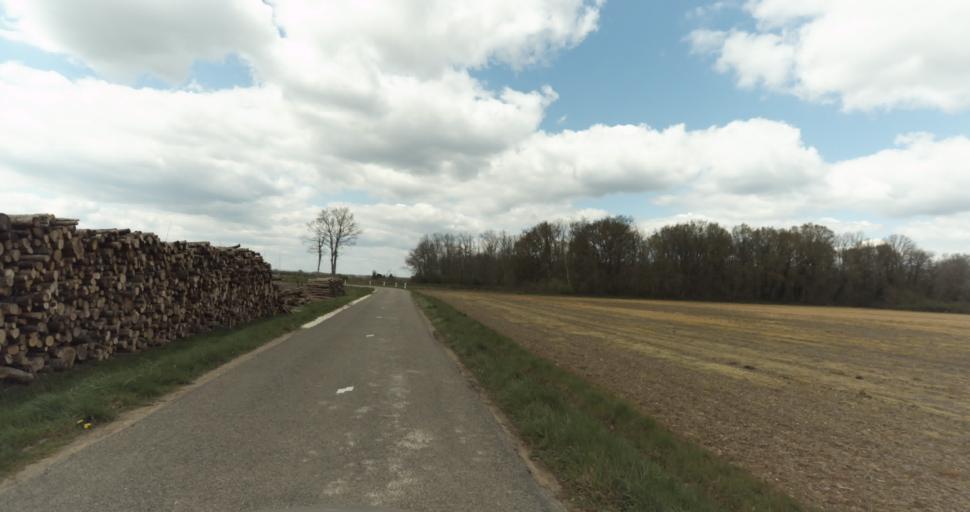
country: FR
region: Bourgogne
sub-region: Departement de la Cote-d'Or
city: Auxonne
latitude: 47.1816
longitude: 5.4168
